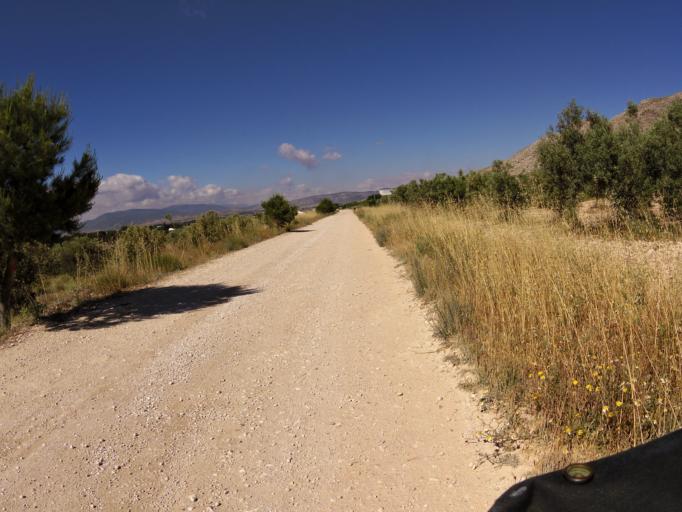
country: ES
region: Valencia
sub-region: Provincia de Alicante
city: Villena
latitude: 38.6340
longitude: -0.8379
